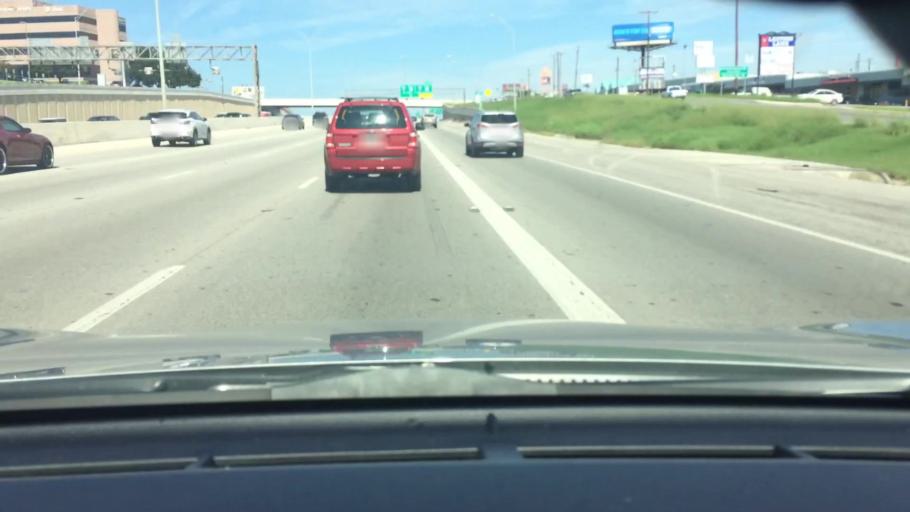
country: US
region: Texas
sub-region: Bexar County
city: Balcones Heights
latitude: 29.4923
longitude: -98.5556
